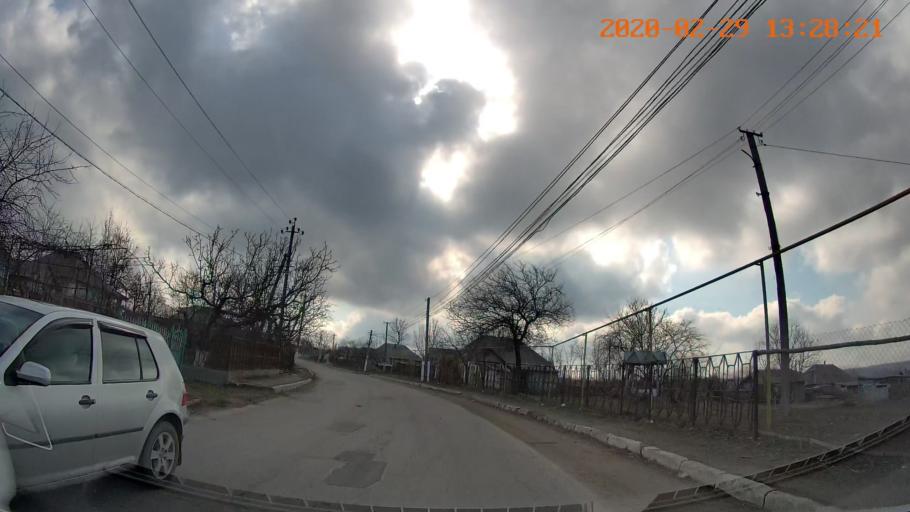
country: MD
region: Telenesti
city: Camenca
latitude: 47.9062
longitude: 28.6424
